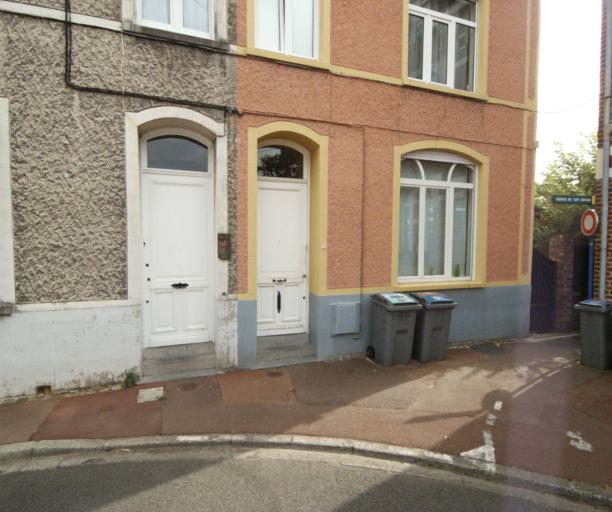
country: FR
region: Nord-Pas-de-Calais
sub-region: Departement du Nord
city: Villeneuve-d'Ascq
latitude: 50.6211
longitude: 3.1609
